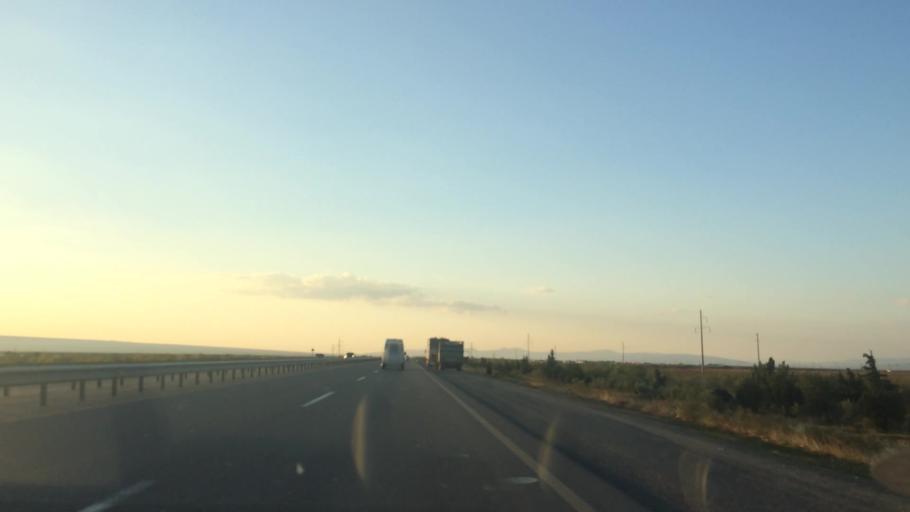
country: AZ
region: Baki
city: Qobustan
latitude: 39.9933
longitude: 49.1912
